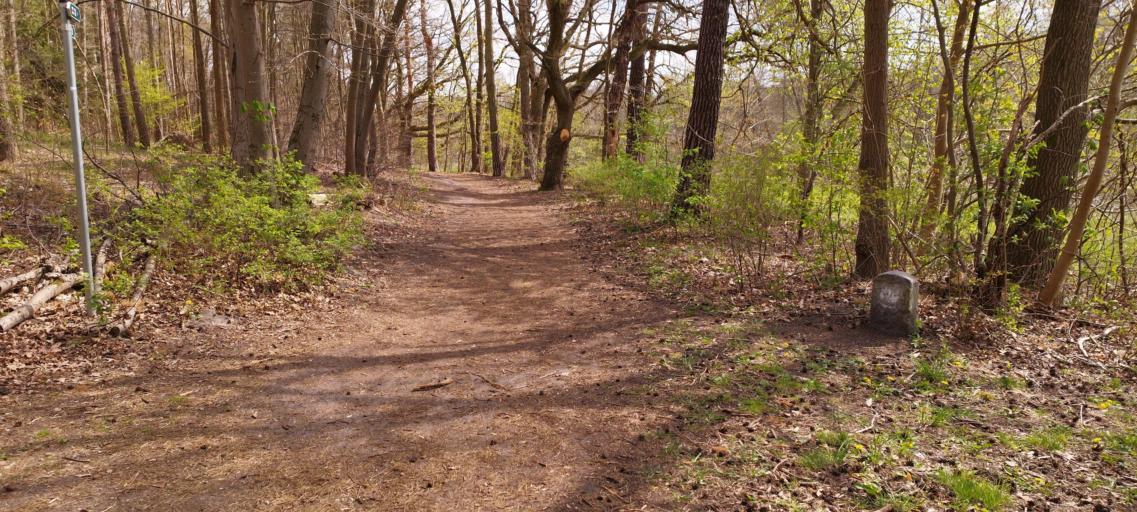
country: DE
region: Brandenburg
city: Erkner
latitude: 52.4193
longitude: 13.7676
